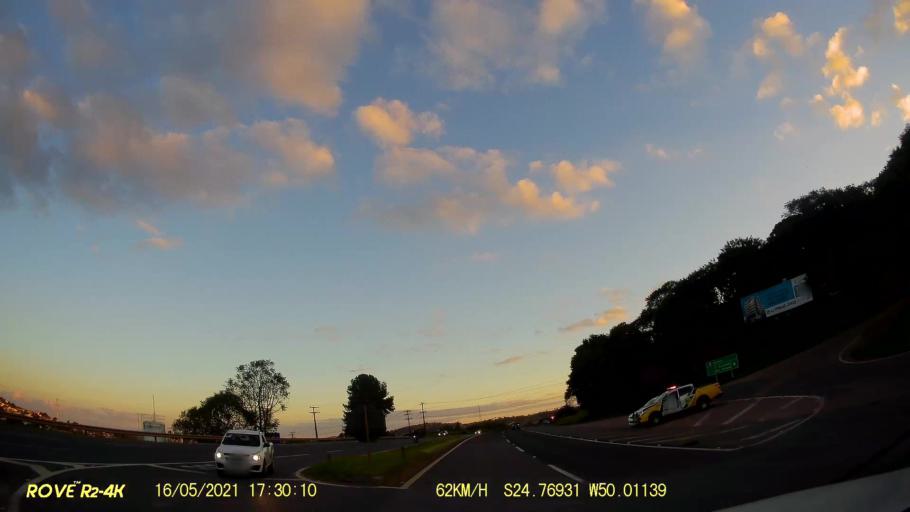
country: BR
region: Parana
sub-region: Castro
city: Castro
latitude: -24.7697
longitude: -50.0117
